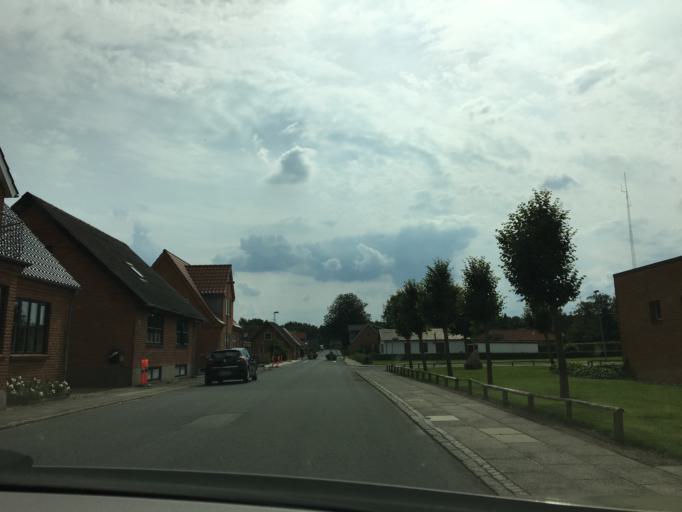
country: DK
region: Central Jutland
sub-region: Viborg Kommune
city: Stoholm
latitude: 56.4832
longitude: 9.1502
